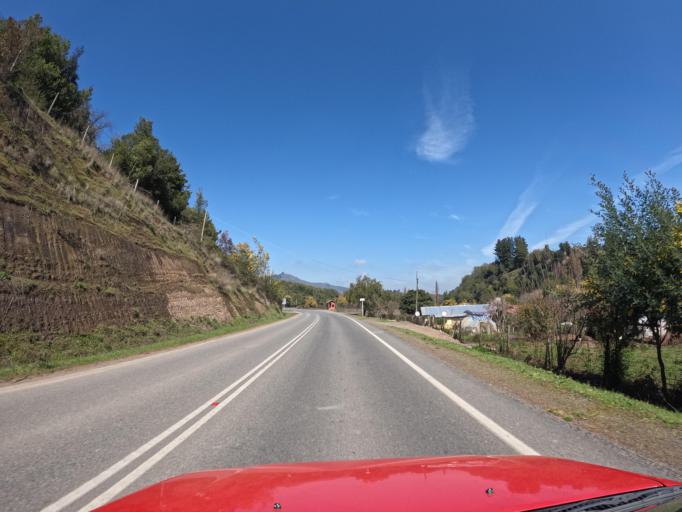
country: CL
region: Maule
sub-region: Provincia de Talca
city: San Clemente
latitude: -35.4605
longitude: -71.2698
